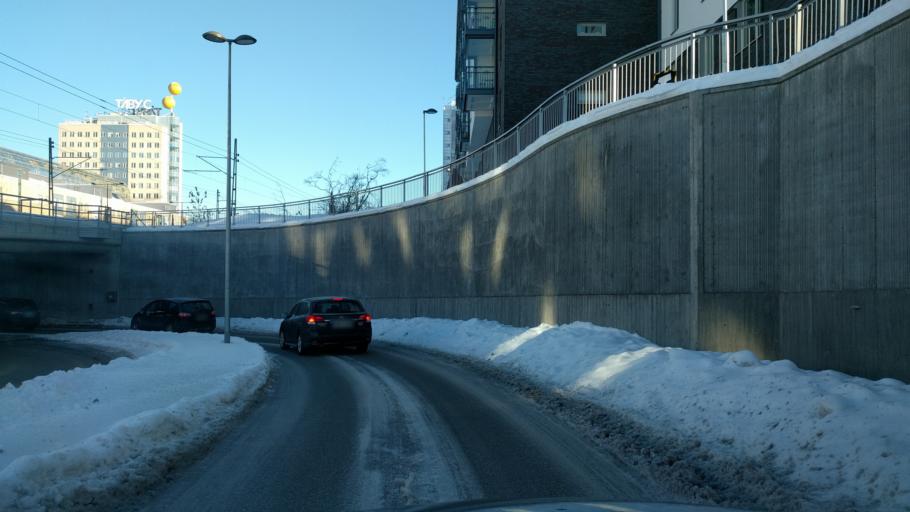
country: SE
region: Stockholm
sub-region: Taby Kommun
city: Taby
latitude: 59.4424
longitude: 18.0712
